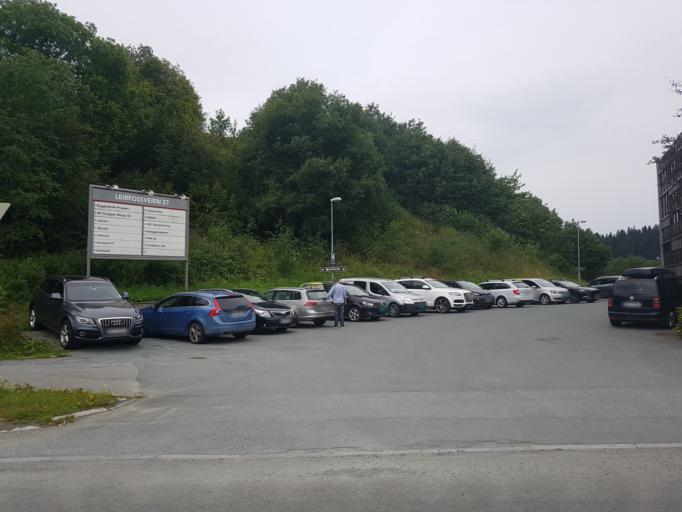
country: NO
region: Sor-Trondelag
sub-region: Trondheim
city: Trondheim
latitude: 63.3904
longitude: 10.3966
